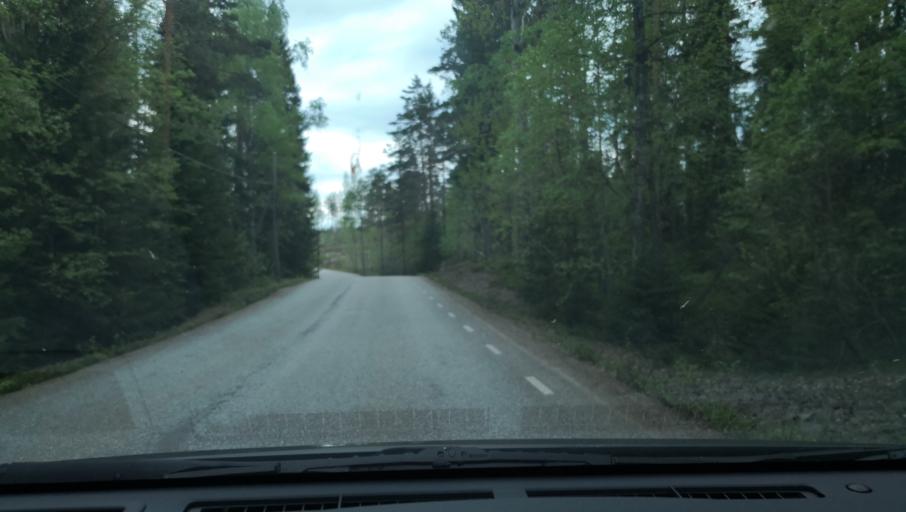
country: SE
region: Vaestmanland
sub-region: Skinnskattebergs Kommun
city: Skinnskatteberg
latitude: 59.8246
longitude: 15.5517
